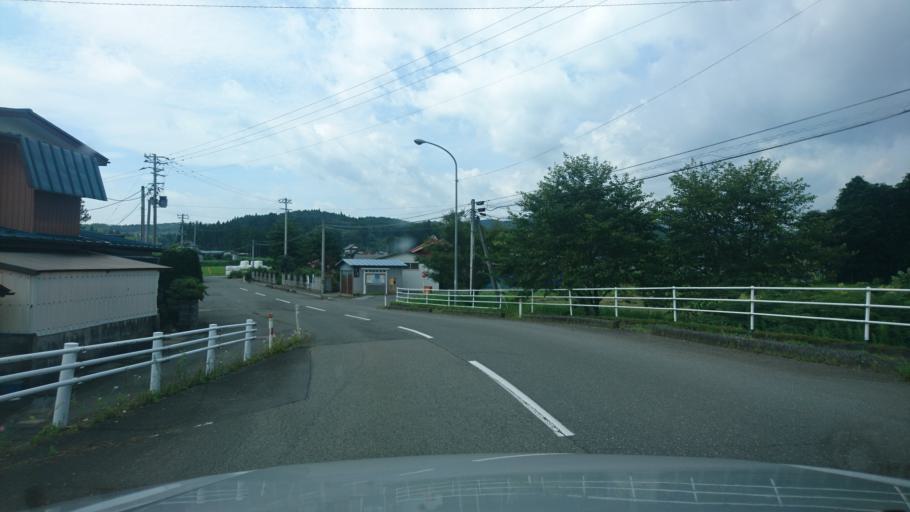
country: JP
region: Iwate
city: Ichinoseki
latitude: 38.8184
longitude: 140.9347
